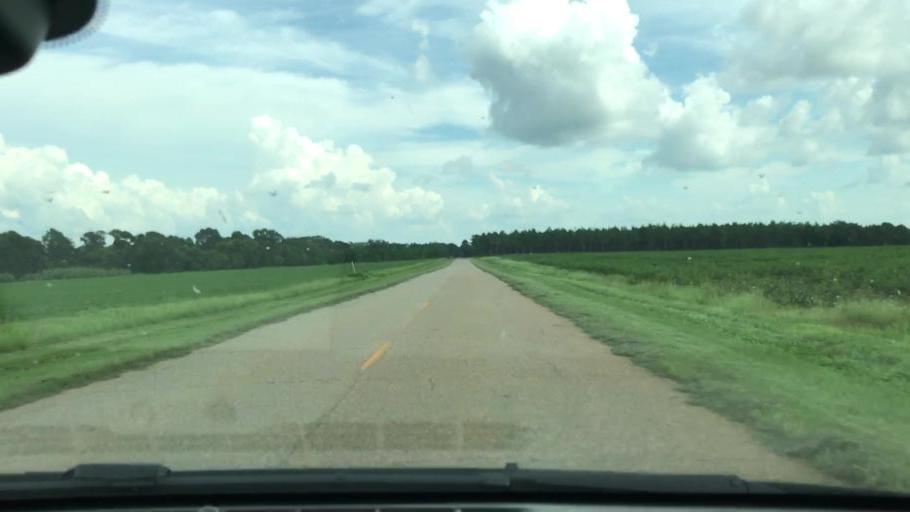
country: US
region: Georgia
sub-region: Clay County
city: Fort Gaines
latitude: 31.5646
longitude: -84.9866
